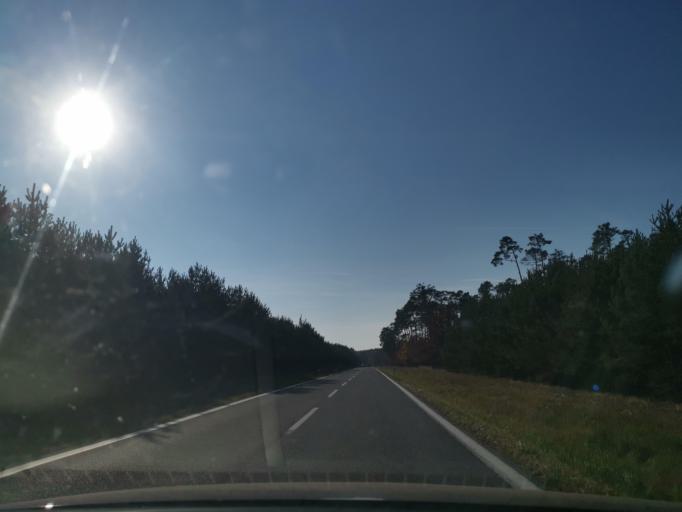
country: SK
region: Bratislavsky
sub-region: Okres Malacky
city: Malacky
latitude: 48.4908
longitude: 17.0824
